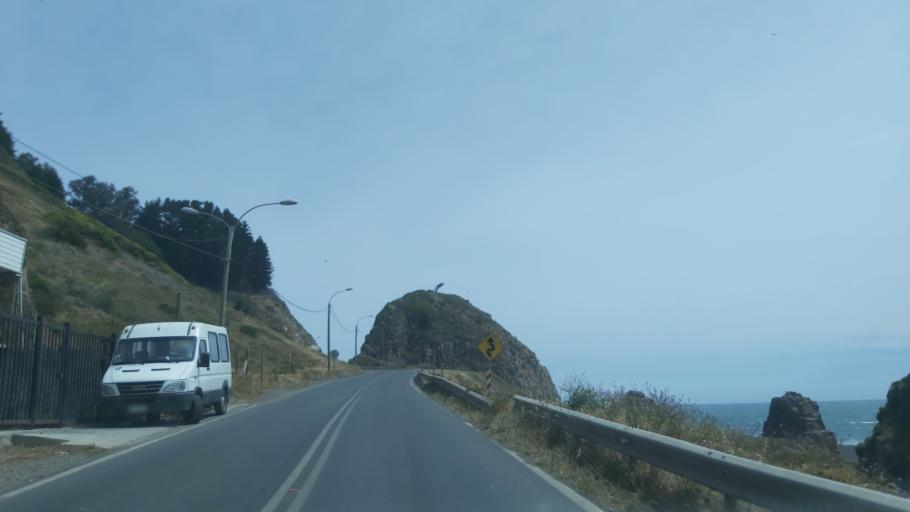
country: CL
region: Maule
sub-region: Provincia de Talca
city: Constitucion
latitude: -35.3287
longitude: -72.4317
